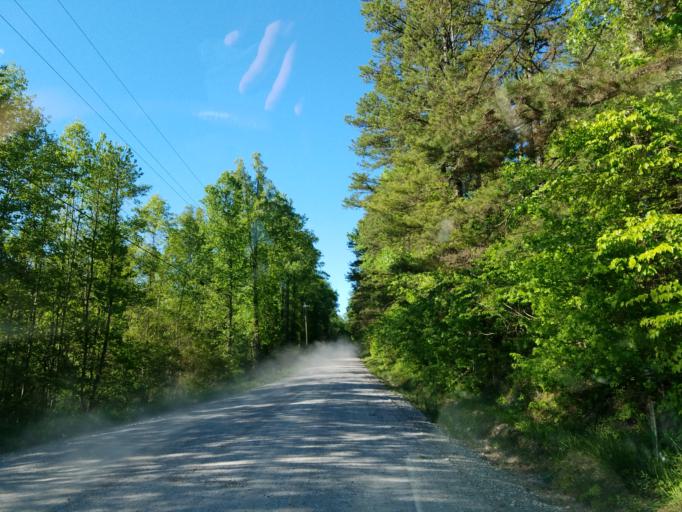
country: US
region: Georgia
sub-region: Gilmer County
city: Ellijay
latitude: 34.6256
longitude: -84.5013
